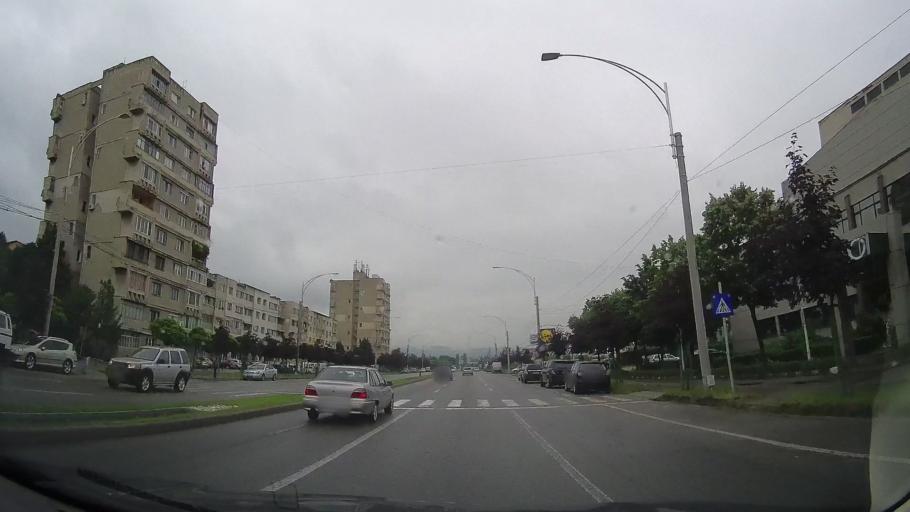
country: RO
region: Mehedinti
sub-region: Municipiul Drobeta-Turnu Severin
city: Drobeta-Turnu Severin
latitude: 44.6324
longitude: 22.6759
